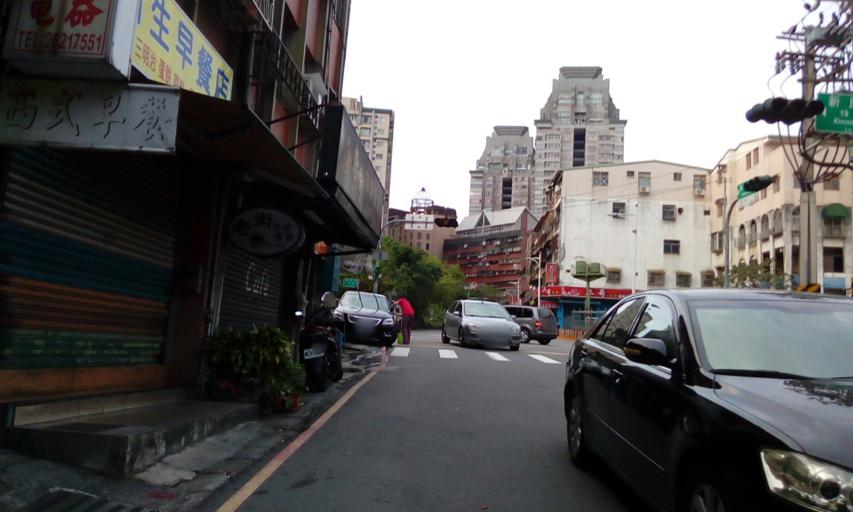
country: TW
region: Taipei
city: Taipei
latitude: 25.1737
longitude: 121.4389
